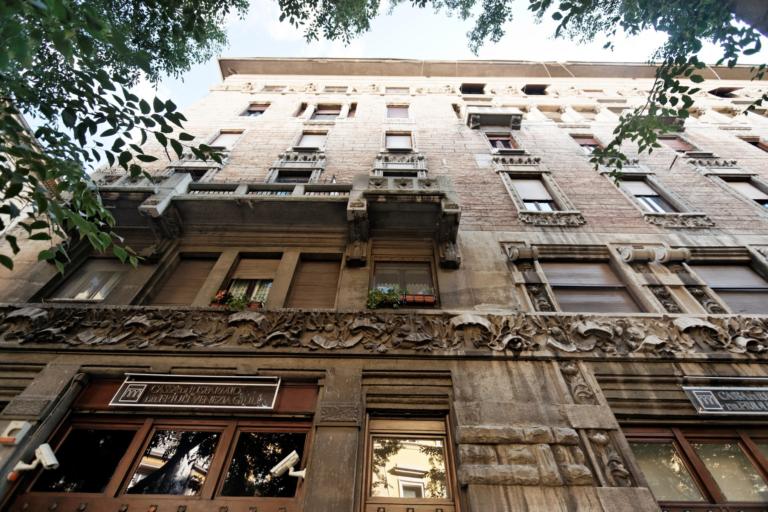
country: IT
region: Friuli Venezia Giulia
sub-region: Provincia di Trieste
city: Trieste
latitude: 45.6522
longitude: 13.7822
